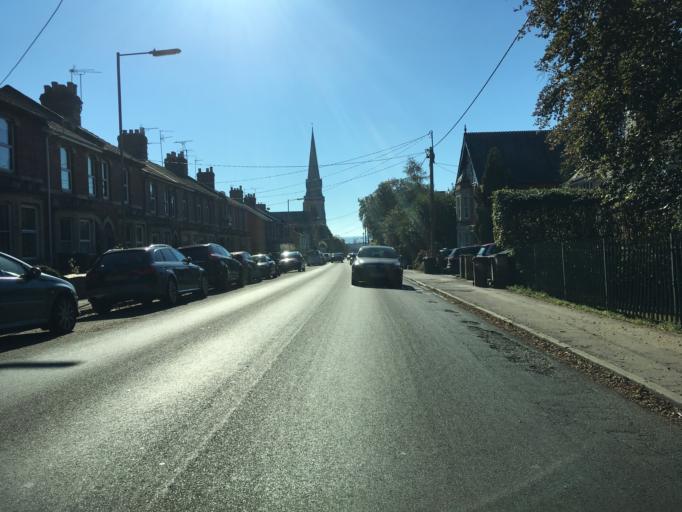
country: GB
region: England
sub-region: Wiltshire
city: Chippenham
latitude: 51.4662
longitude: -2.1195
